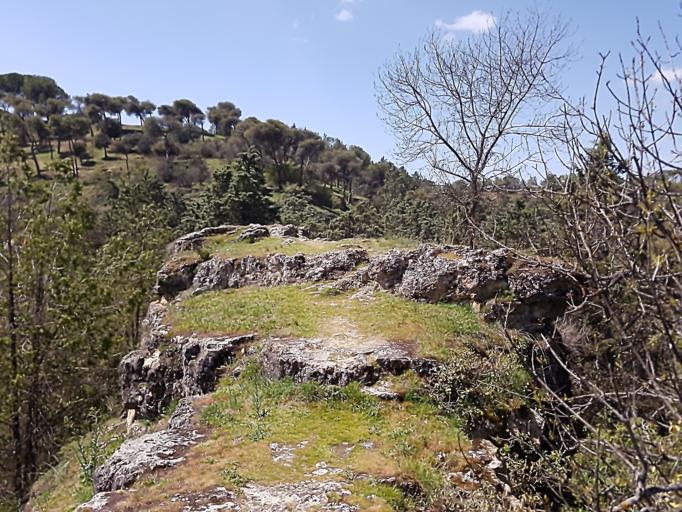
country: ES
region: Castille and Leon
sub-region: Provincia de Segovia
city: Segovia
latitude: 40.9509
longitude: -4.1304
